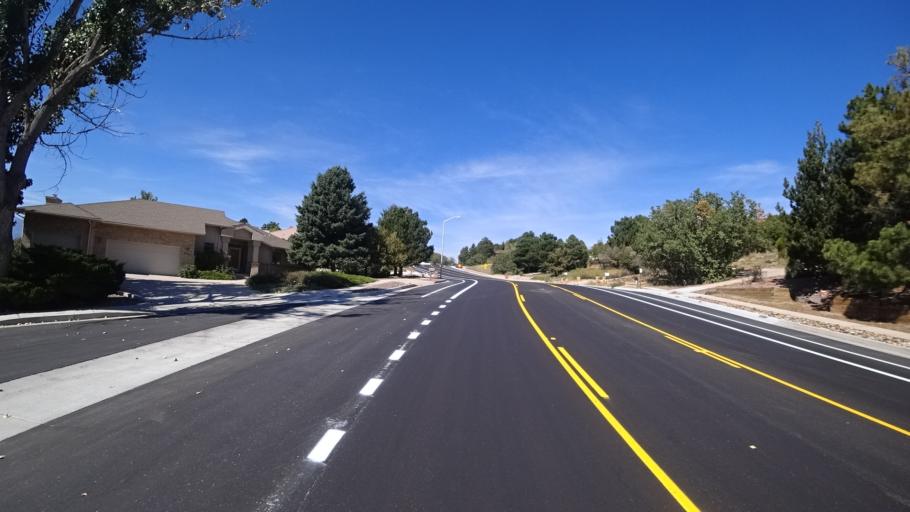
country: US
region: Colorado
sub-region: El Paso County
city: Cimarron Hills
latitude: 38.9138
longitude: -104.7612
